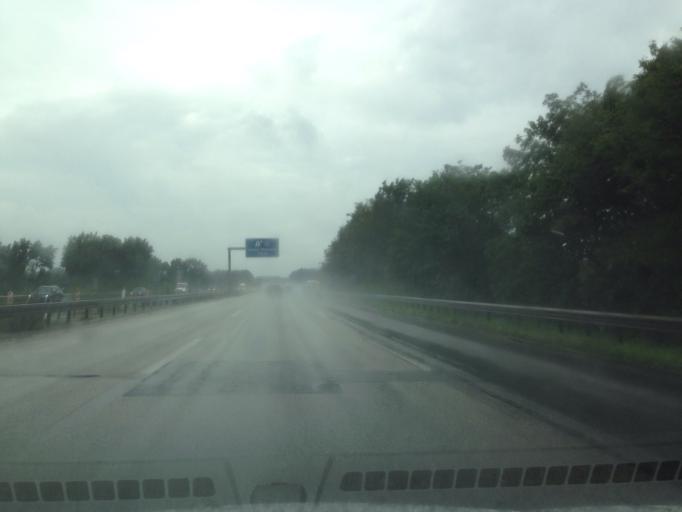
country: DE
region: North Rhine-Westphalia
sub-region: Regierungsbezirk Dusseldorf
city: Hochfeld
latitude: 51.4358
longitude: 6.6949
